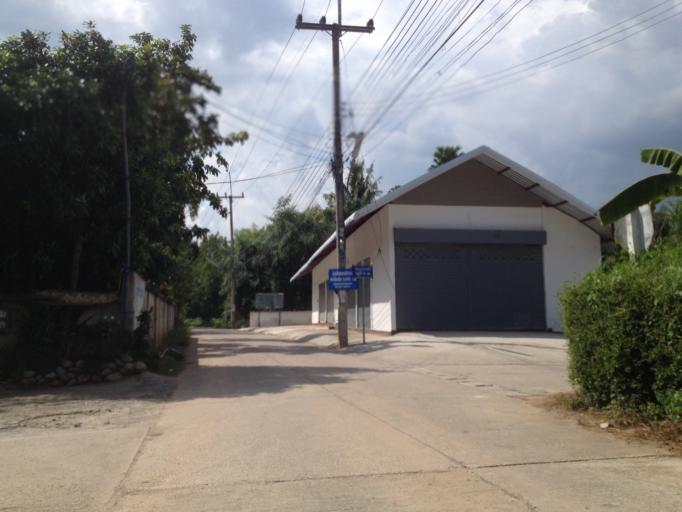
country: TH
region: Chiang Mai
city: Hang Dong
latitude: 18.7391
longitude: 98.9281
